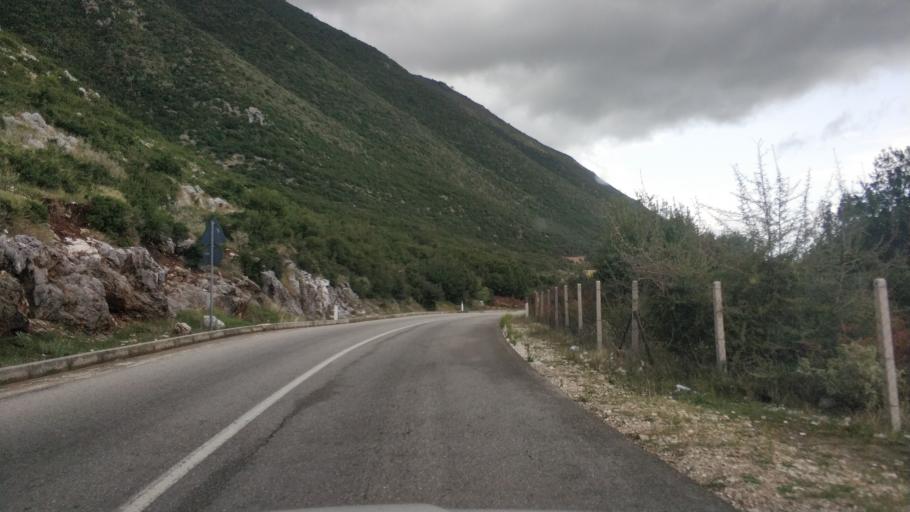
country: AL
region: Vlore
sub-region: Rrethi i Vlores
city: Brataj
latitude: 40.2326
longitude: 19.5582
